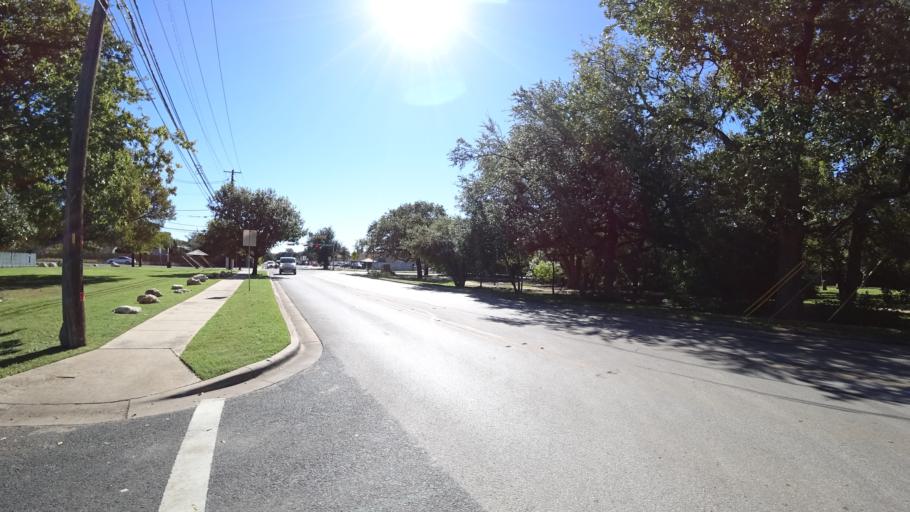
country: US
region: Texas
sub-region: Travis County
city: Rollingwood
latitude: 30.2260
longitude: -97.8045
